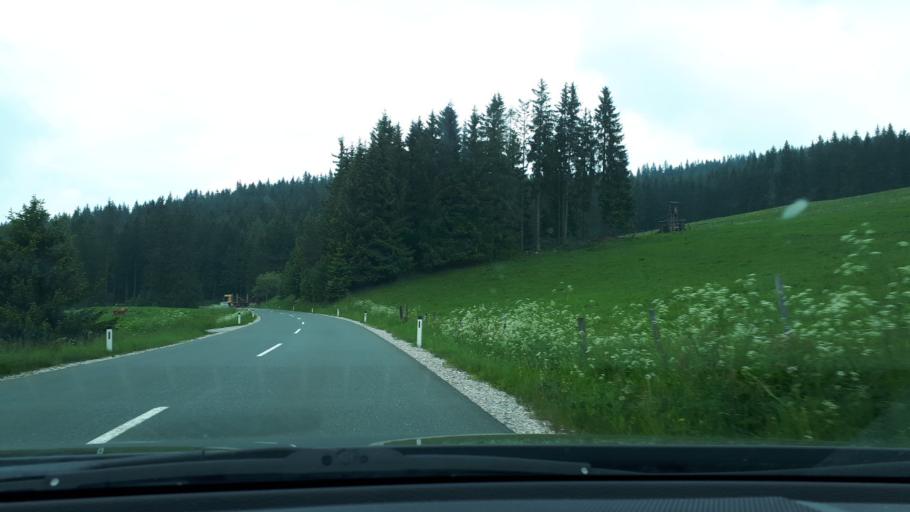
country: AT
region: Styria
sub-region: Politischer Bezirk Voitsberg
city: Pack
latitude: 46.9300
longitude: 14.9947
